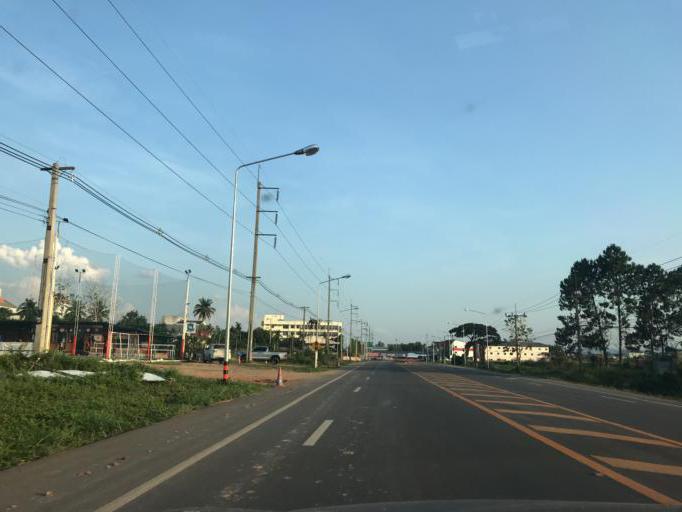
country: TH
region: Phayao
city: Chiang Kham
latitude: 19.5214
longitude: 100.2953
